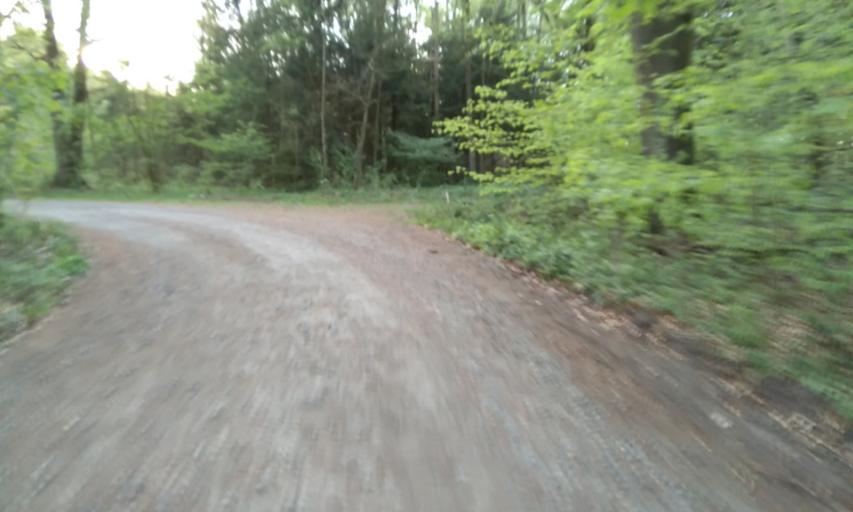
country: DE
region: Lower Saxony
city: Nottensdorf
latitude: 53.4913
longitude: 9.6156
